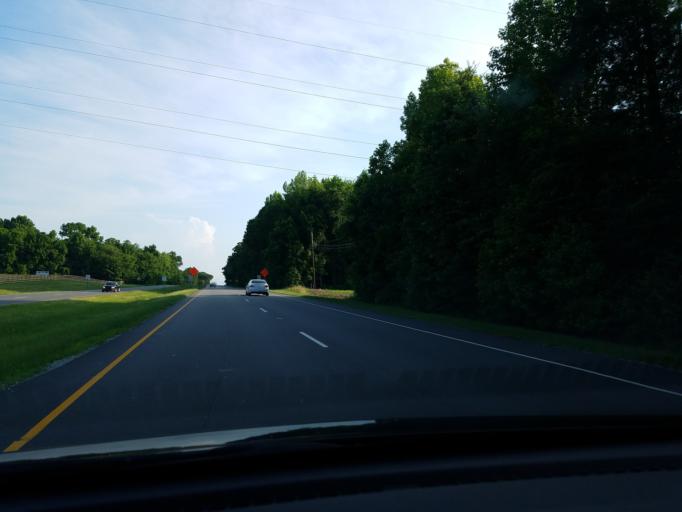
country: US
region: North Carolina
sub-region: Durham County
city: Gorman
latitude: 36.1211
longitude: -78.9016
